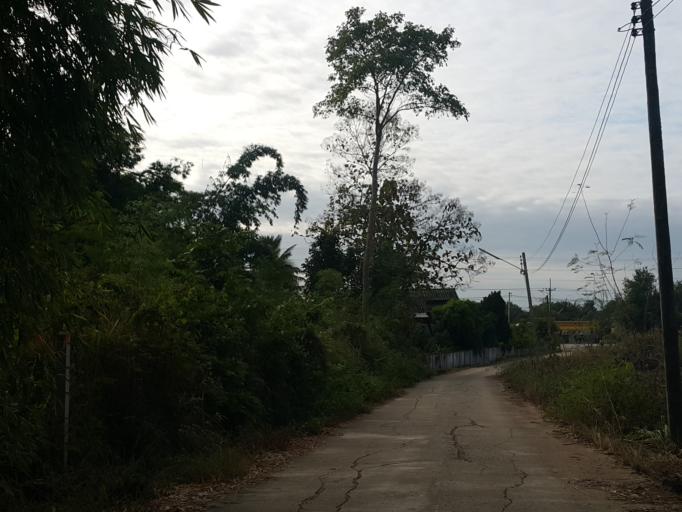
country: TH
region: Lampang
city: Mae Mo
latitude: 18.2486
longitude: 99.5980
